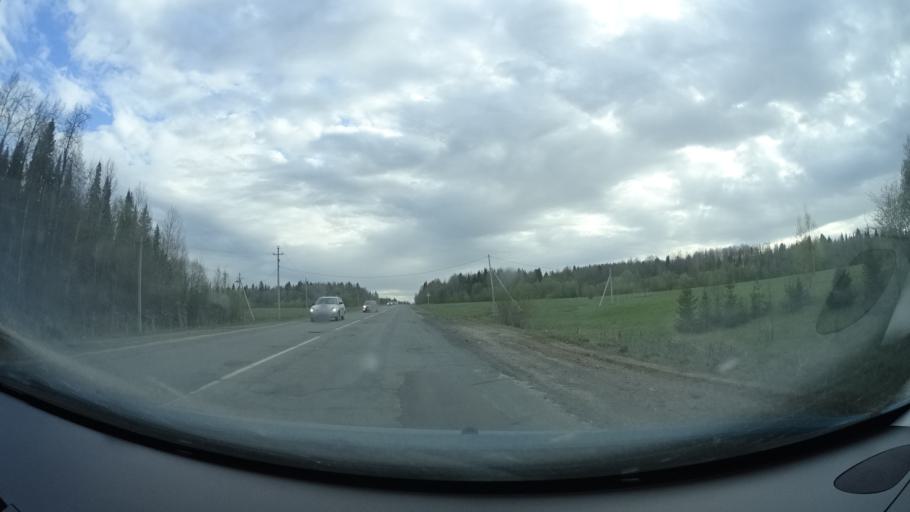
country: RU
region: Perm
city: Kultayevo
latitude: 57.8279
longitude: 55.8110
